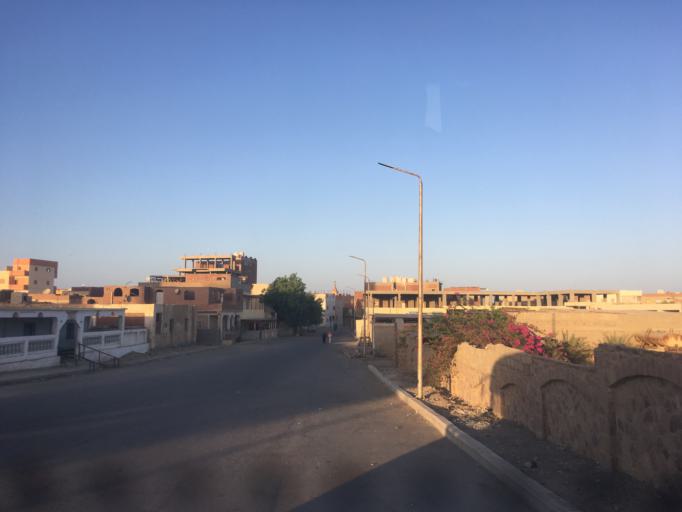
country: EG
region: Red Sea
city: Al Qusayr
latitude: 26.1089
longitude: 34.2806
